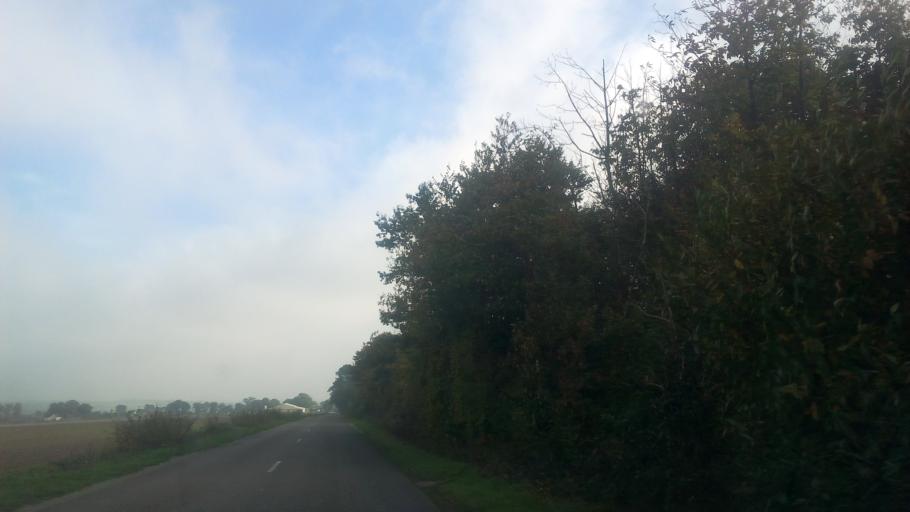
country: FR
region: Pays de la Loire
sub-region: Departement de la Loire-Atlantique
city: Guemene-Penfao
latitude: 47.6288
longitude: -1.8036
